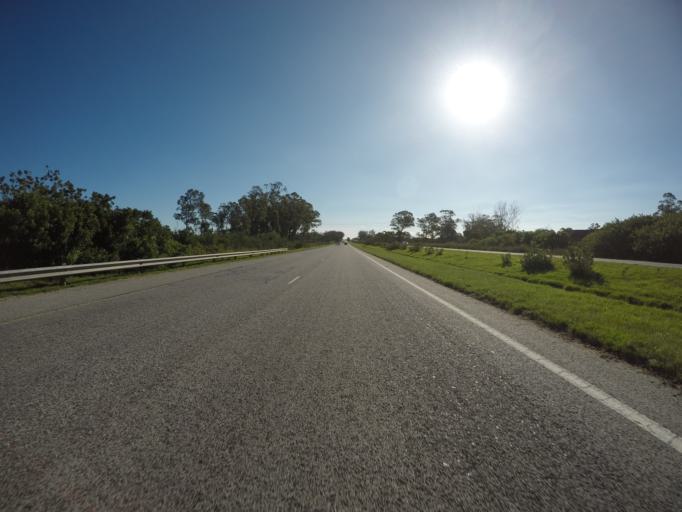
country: ZA
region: Eastern Cape
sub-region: Nelson Mandela Bay Metropolitan Municipality
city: Uitenhage
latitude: -33.9386
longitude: 25.3743
